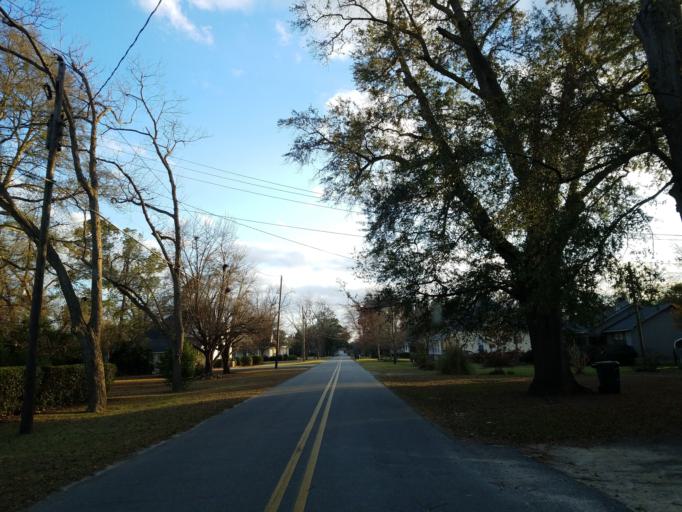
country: US
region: Georgia
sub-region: Dooly County
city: Unadilla
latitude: 32.1957
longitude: -83.7645
